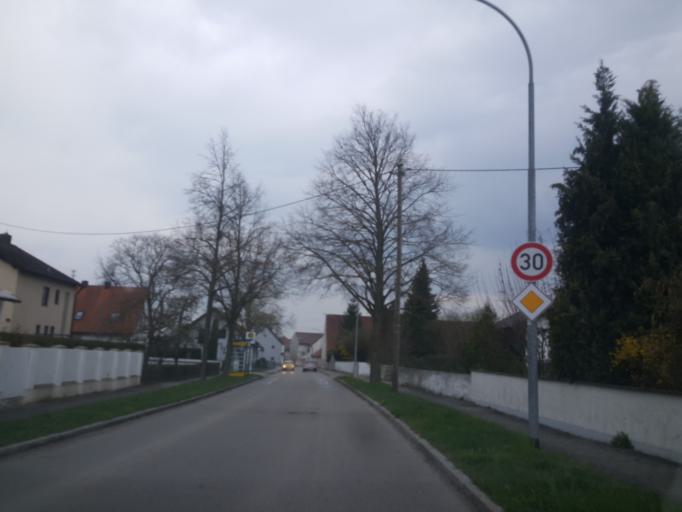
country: DE
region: Bavaria
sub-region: Upper Bavaria
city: Buxheim
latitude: 48.7778
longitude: 11.3083
